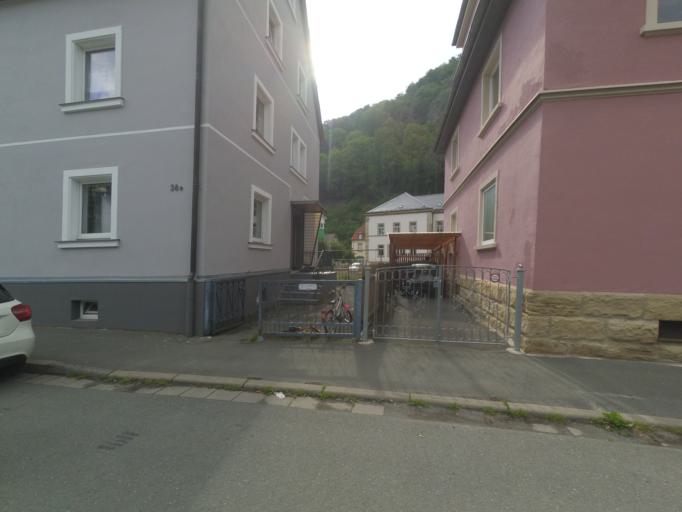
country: DE
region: Bavaria
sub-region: Upper Franconia
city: Bad Berneck im Fichtelgebirge
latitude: 50.0457
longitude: 11.6710
